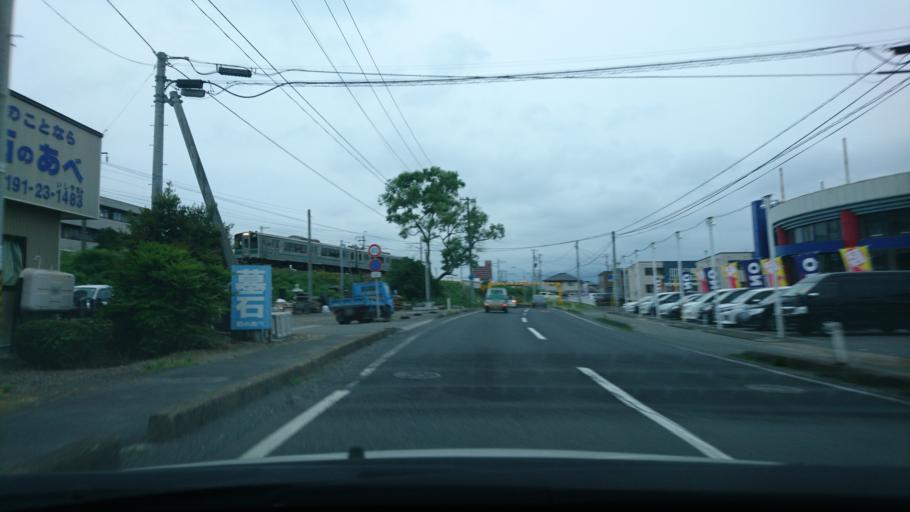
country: JP
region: Iwate
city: Ichinoseki
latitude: 38.9124
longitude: 141.1314
